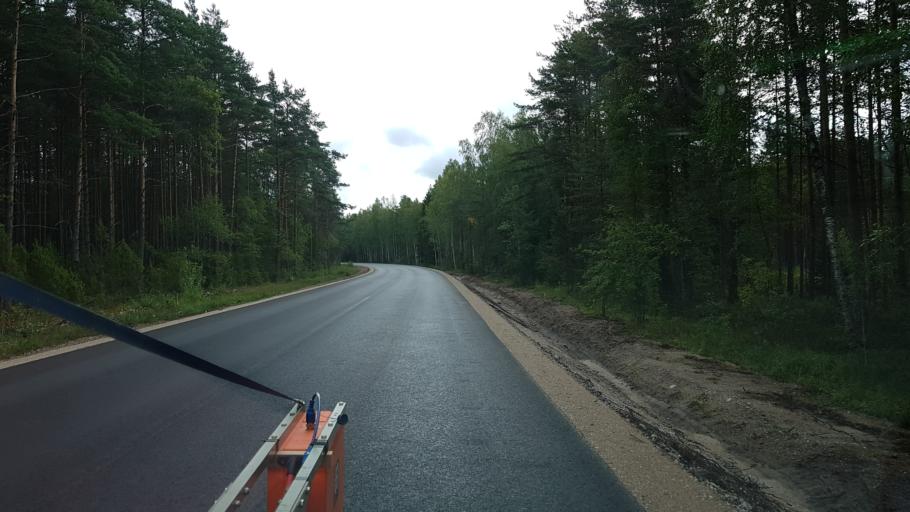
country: EE
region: Harju
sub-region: Nissi vald
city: Turba
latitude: 59.0868
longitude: 23.9499
